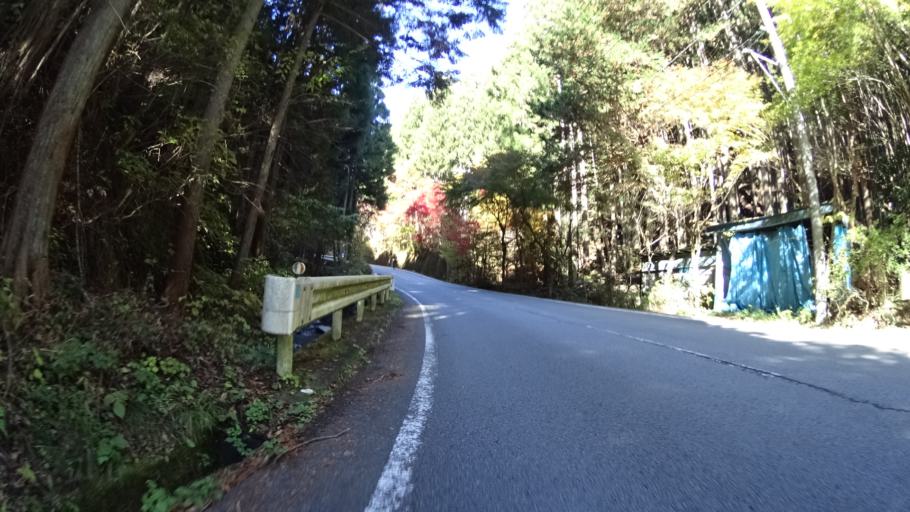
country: JP
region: Yamanashi
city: Otsuki
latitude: 35.7644
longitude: 138.9371
